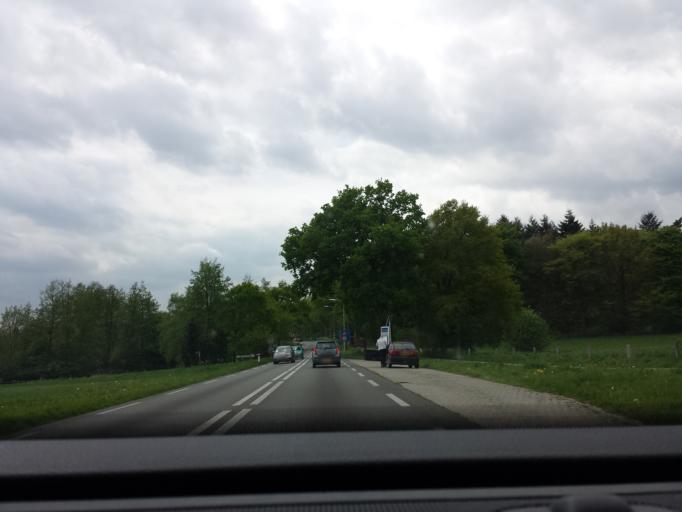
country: NL
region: Gelderland
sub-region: Gemeente Montferland
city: s-Heerenberg
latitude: 51.8866
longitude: 6.2521
